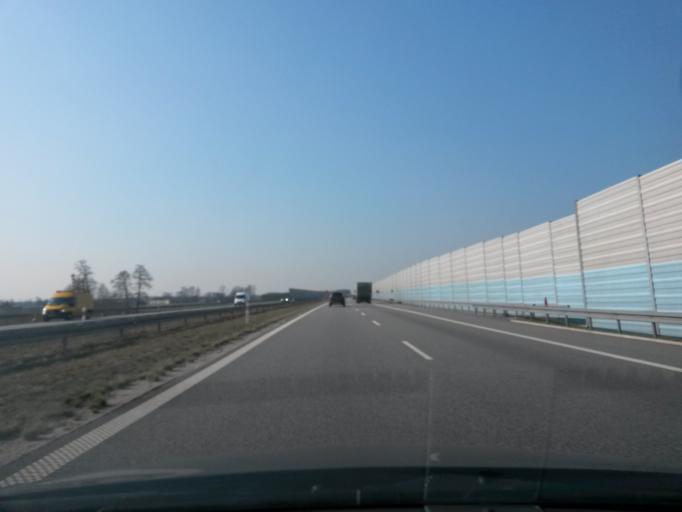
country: PL
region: Lodz Voivodeship
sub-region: powiat Lowicki
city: Lyszkowice
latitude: 51.9716
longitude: 19.8704
